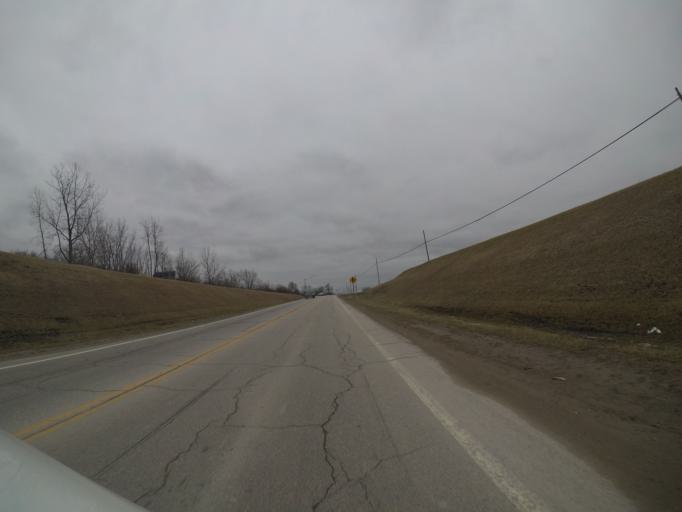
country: US
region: Ohio
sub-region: Wood County
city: Walbridge
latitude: 41.6044
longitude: -83.5123
